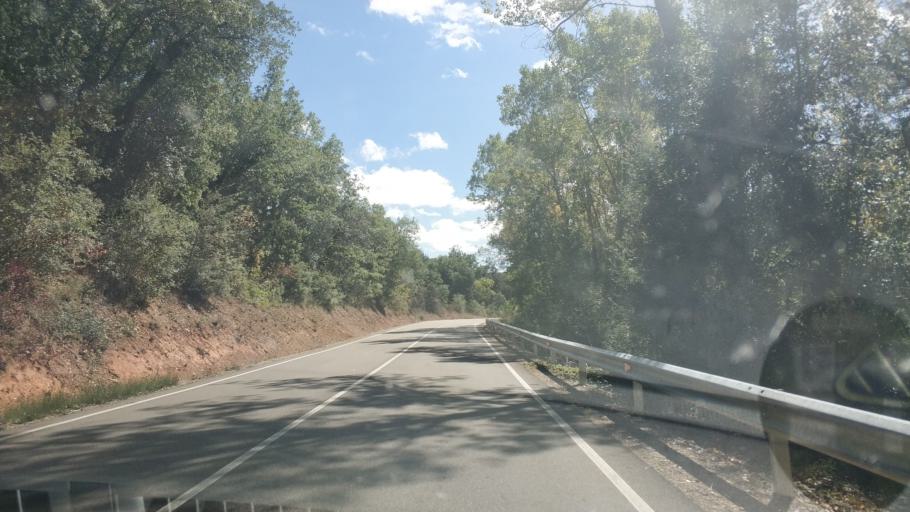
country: ES
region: Castille and Leon
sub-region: Provincia de Burgos
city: Puentedura
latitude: 42.0508
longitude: -3.5511
